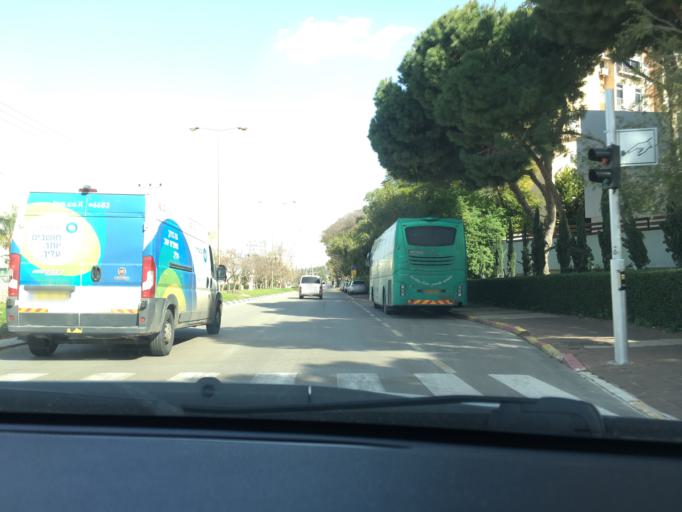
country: IL
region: Central District
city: Kfar Saba
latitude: 32.1843
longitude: 34.9014
